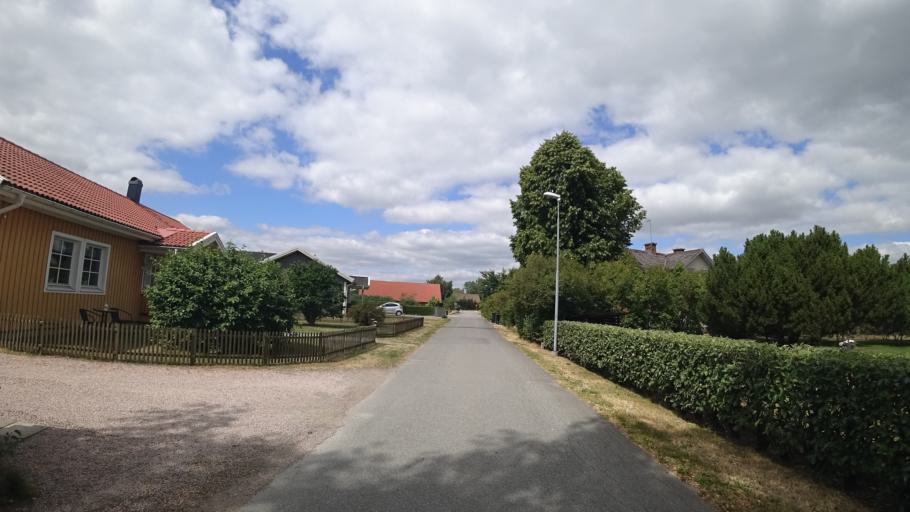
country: SE
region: Skane
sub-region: Kristianstads Kommun
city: Ahus
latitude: 55.9811
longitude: 14.2739
